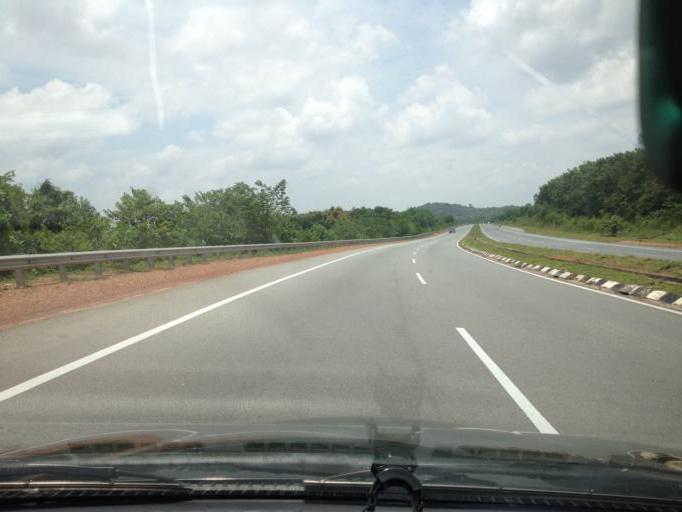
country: MY
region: Kedah
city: Sungai Petani
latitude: 5.6116
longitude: 100.5650
